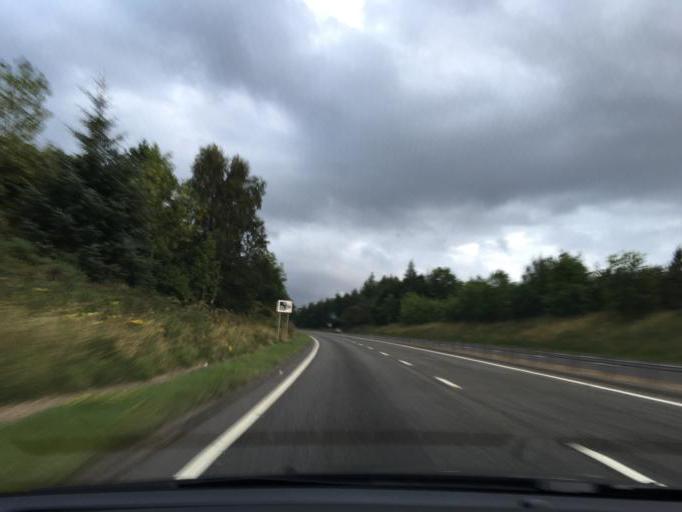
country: GB
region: Scotland
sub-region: Highland
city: Inverness
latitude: 57.4574
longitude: -4.1657
